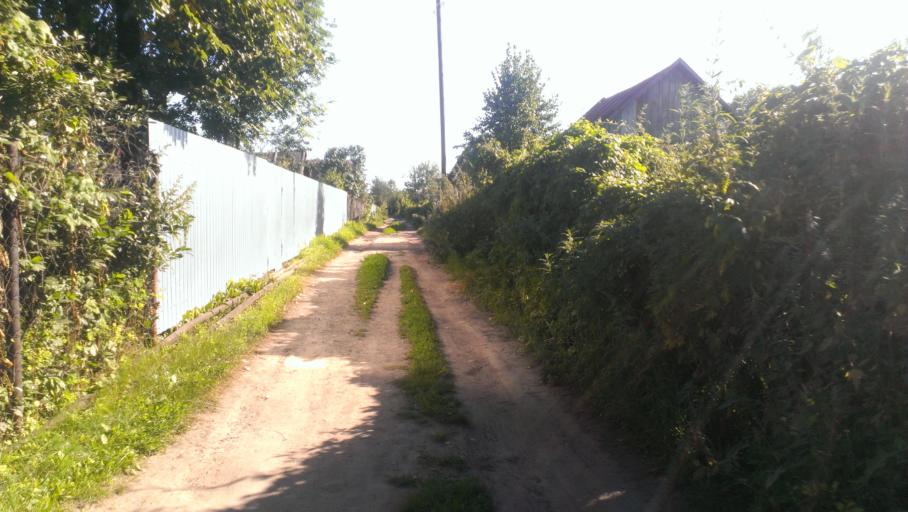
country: RU
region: Altai Krai
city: Novosilikatnyy
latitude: 53.3245
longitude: 83.6697
